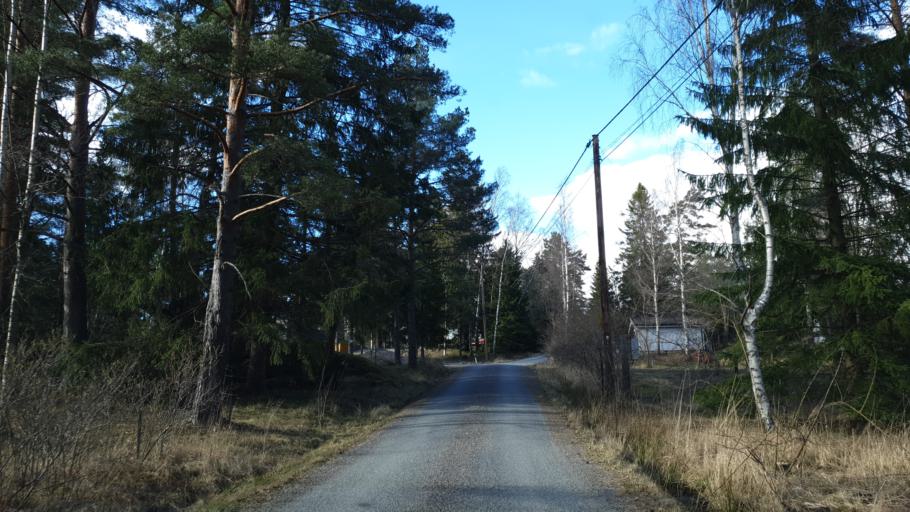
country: SE
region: Stockholm
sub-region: Varmdo Kommun
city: Holo
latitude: 59.2774
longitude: 18.6358
